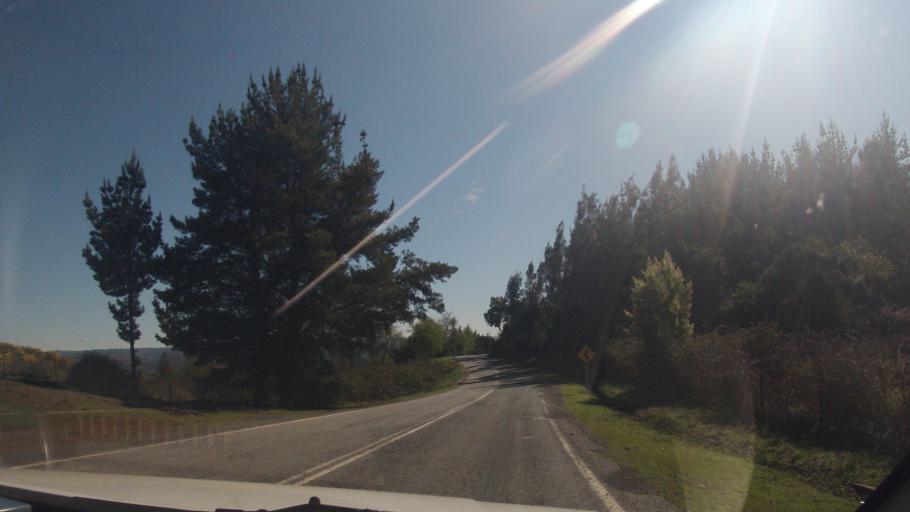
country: CL
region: Araucania
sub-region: Provincia de Malleco
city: Traiguen
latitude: -38.1689
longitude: -72.8604
